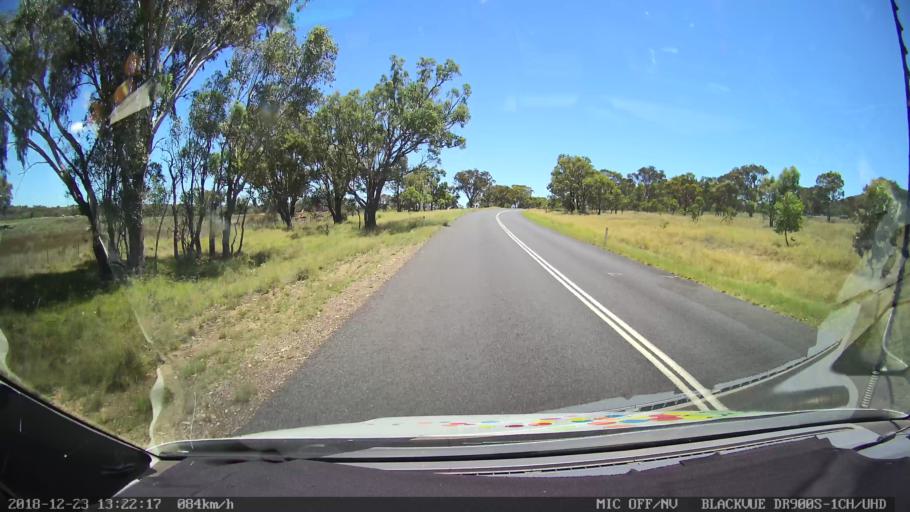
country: AU
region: New South Wales
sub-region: Armidale Dumaresq
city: Armidale
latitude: -30.4786
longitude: 151.4233
